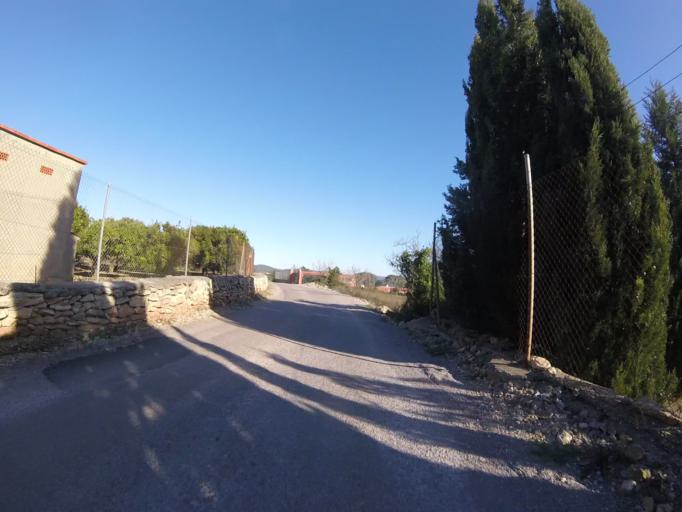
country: ES
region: Valencia
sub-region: Provincia de Castello
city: Alcala de Xivert
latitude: 40.2911
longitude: 0.2166
